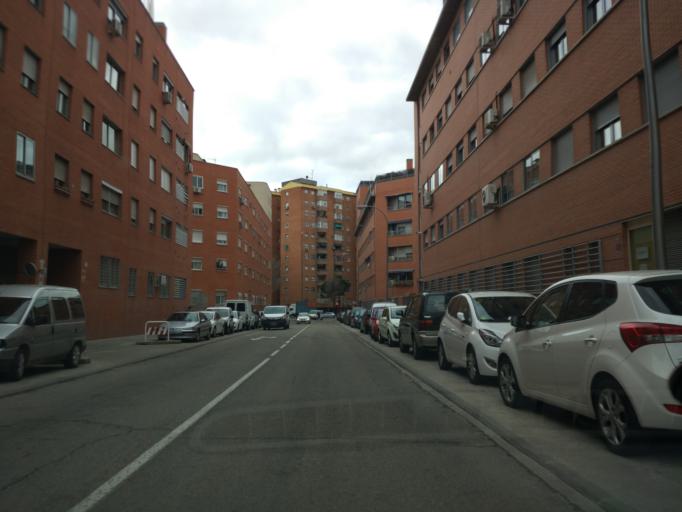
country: ES
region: Madrid
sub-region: Provincia de Madrid
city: San Blas
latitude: 40.4210
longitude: -3.6124
